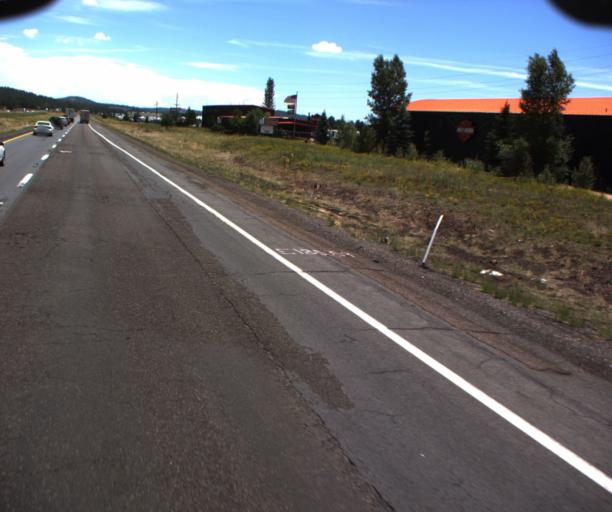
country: US
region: Arizona
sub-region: Coconino County
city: Parks
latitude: 35.2332
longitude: -111.8168
